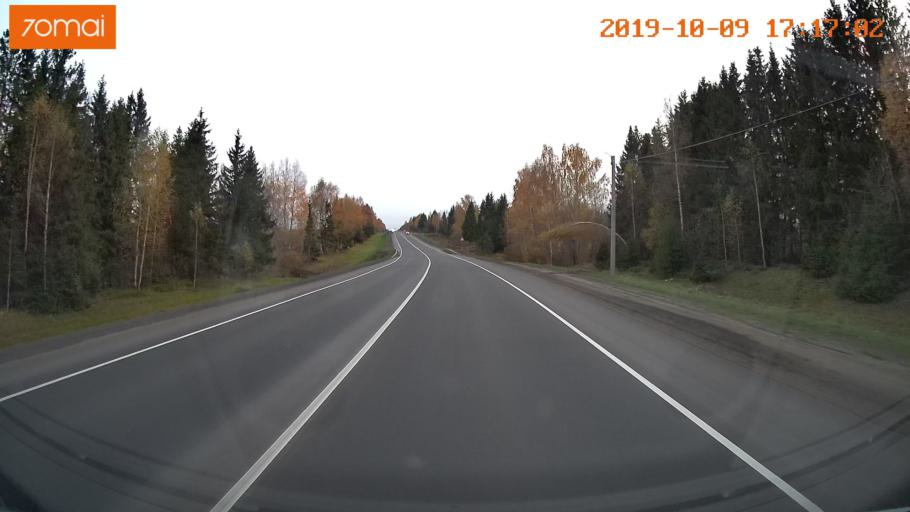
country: RU
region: Ivanovo
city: Furmanov
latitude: 57.2814
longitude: 41.1592
